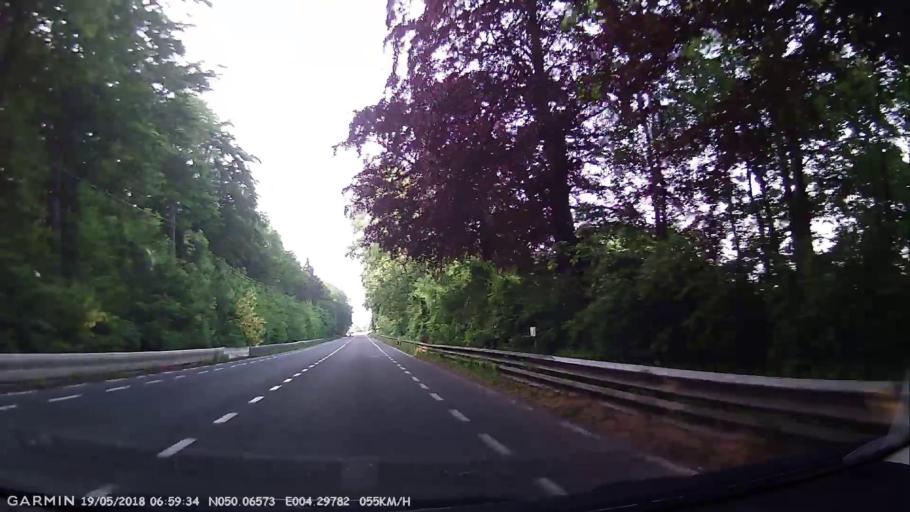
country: BE
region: Wallonia
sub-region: Province du Hainaut
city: Chimay
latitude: 50.0655
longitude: 4.2979
